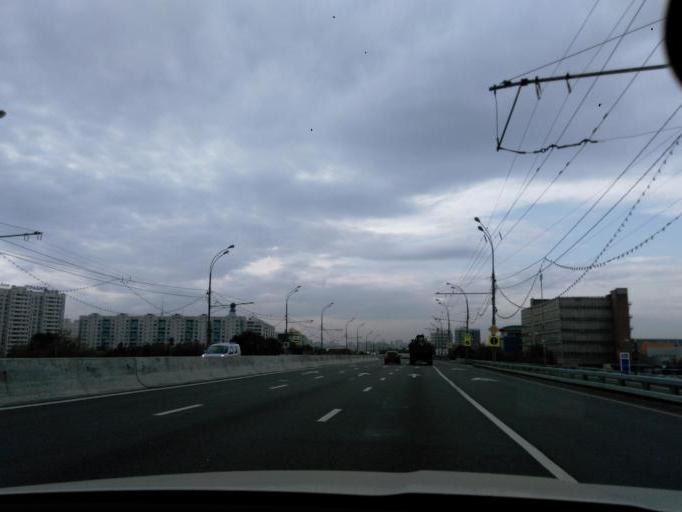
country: RU
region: Moscow
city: Slobodka
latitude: 55.8714
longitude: 37.5855
